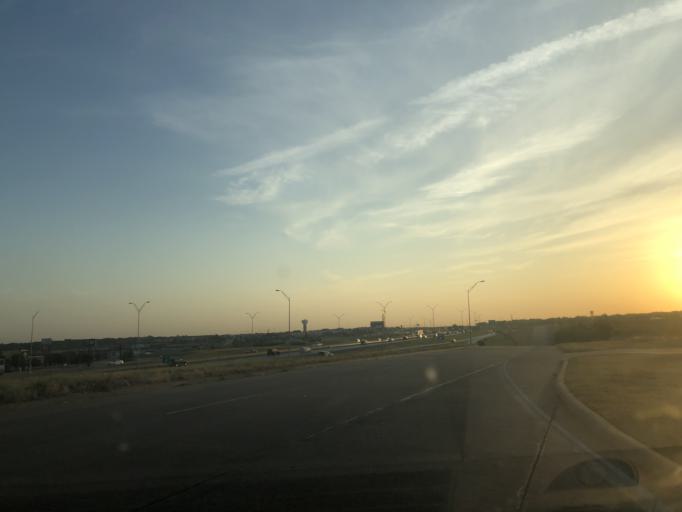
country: US
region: Texas
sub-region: Tarrant County
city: Lake Worth
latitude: 32.8032
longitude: -97.4253
